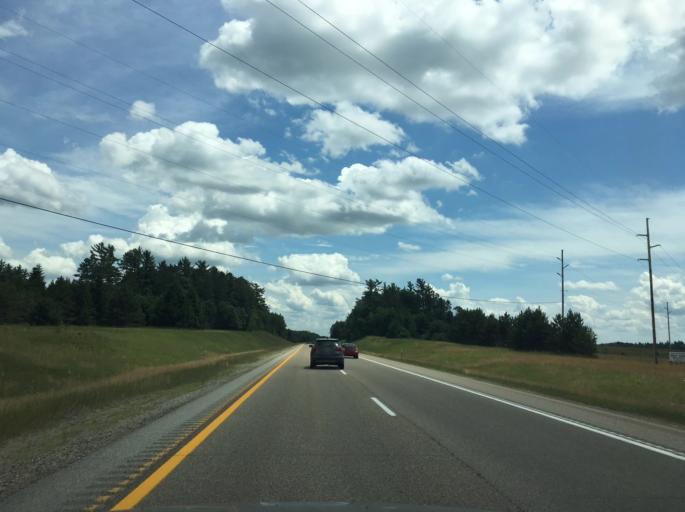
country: US
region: Michigan
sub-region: Roscommon County
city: Roscommon
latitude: 44.5388
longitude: -84.6904
